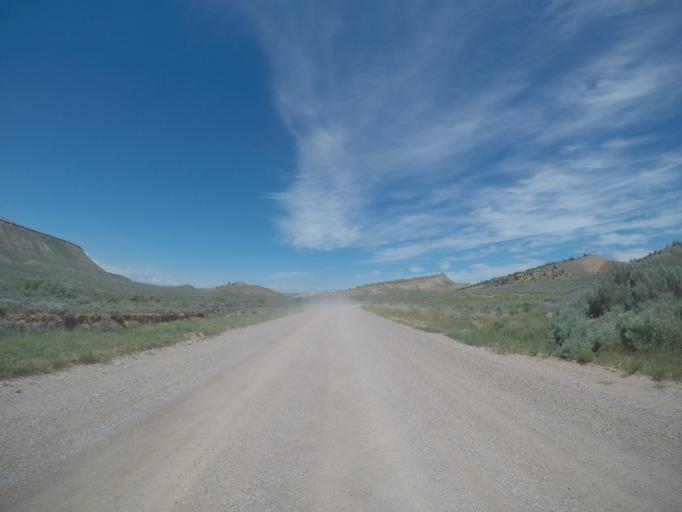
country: US
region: Montana
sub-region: Carbon County
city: Red Lodge
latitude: 45.2051
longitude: -108.8250
